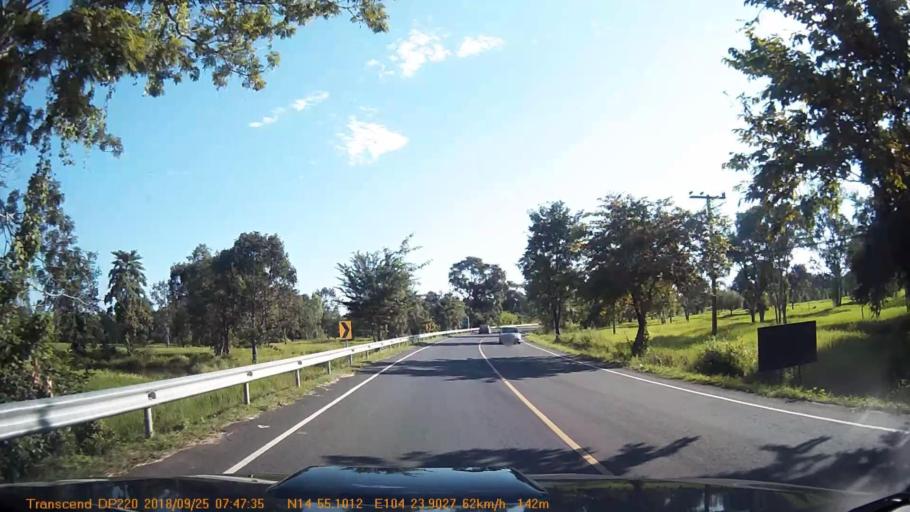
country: TH
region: Sisaket
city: Phayu
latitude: 14.9185
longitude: 104.3985
